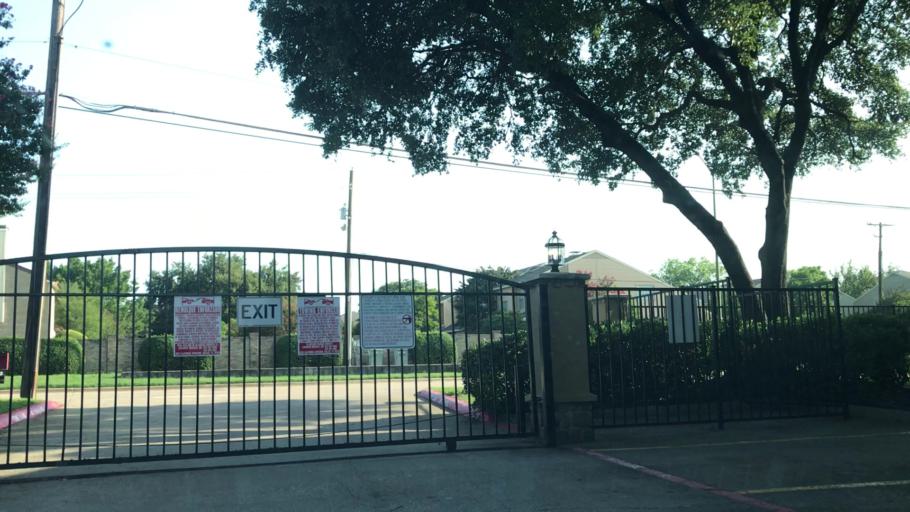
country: US
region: Texas
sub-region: Dallas County
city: Addison
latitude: 32.9391
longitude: -96.8066
